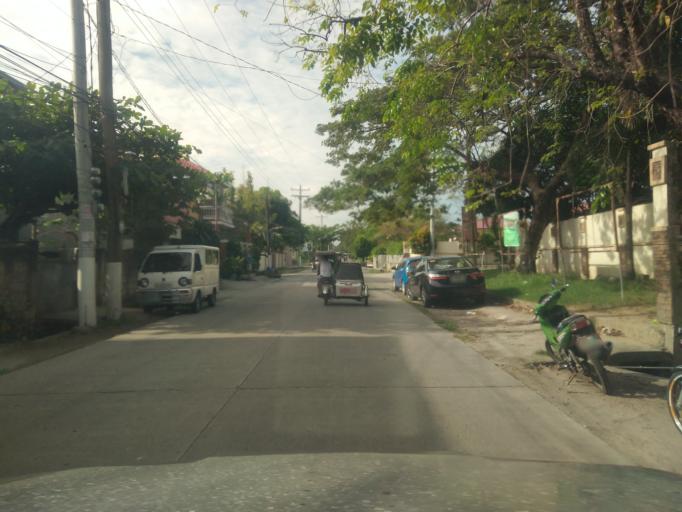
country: PH
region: Central Luzon
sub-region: Province of Pampanga
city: Guagua
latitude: 14.9547
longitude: 120.6295
